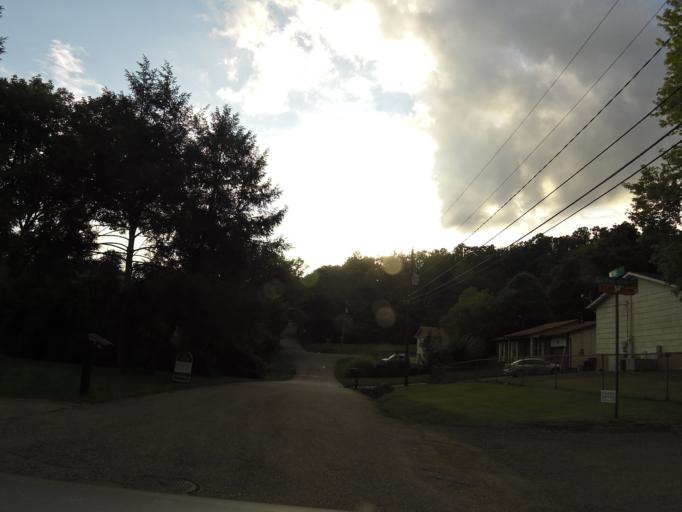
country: US
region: Tennessee
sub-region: Knox County
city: Knoxville
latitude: 35.9911
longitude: -83.9807
